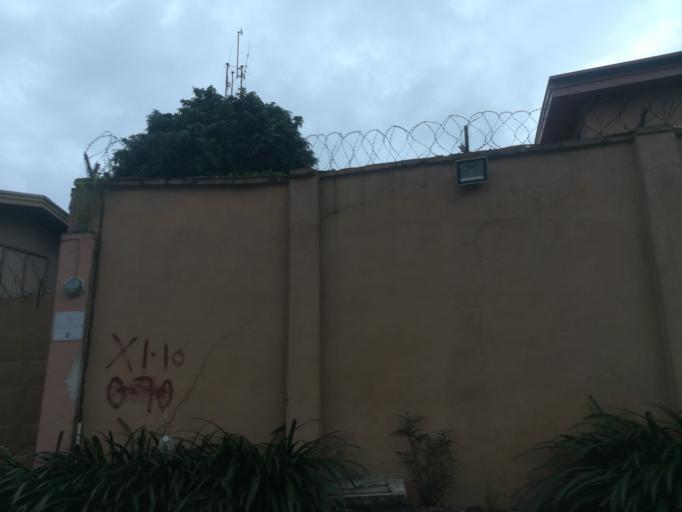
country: NG
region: Lagos
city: Lagos
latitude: 6.4420
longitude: 3.4125
